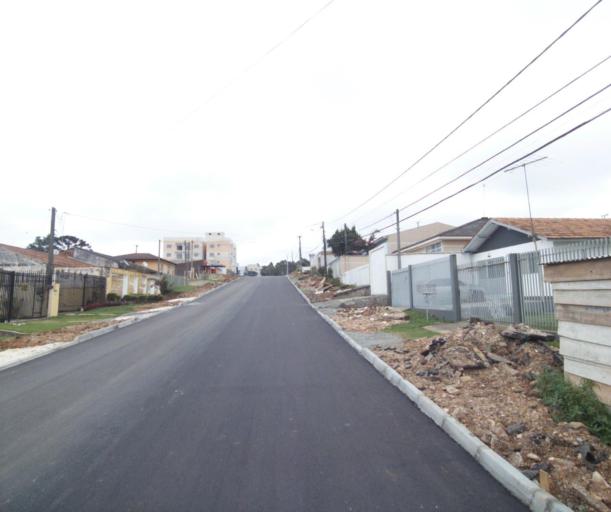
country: BR
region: Parana
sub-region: Quatro Barras
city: Quatro Barras
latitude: -25.3634
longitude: -49.1123
